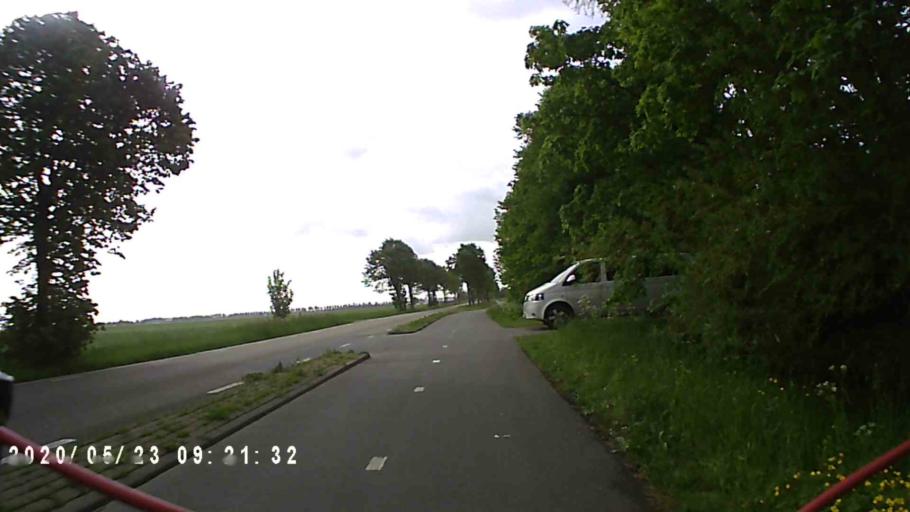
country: NL
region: Groningen
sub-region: Gemeente Bedum
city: Bedum
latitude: 53.2928
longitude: 6.6770
